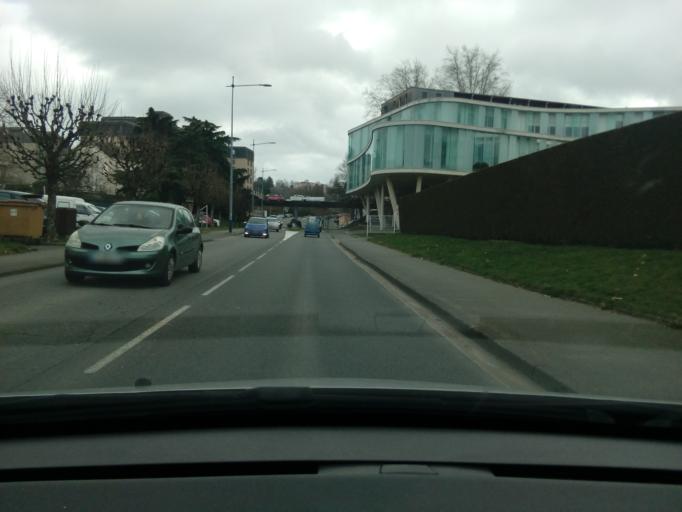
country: FR
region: Limousin
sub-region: Departement de la Creuse
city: Gueret
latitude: 46.1725
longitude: 1.8739
